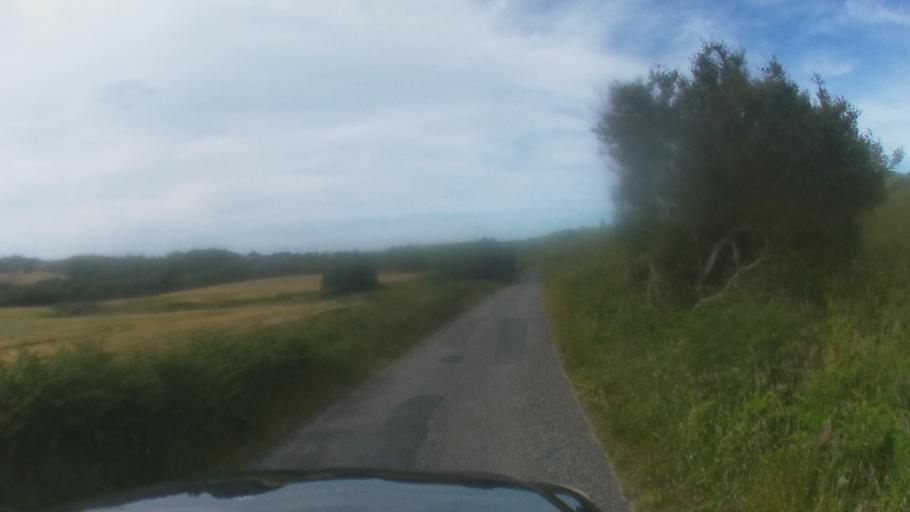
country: IE
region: Leinster
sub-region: Loch Garman
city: Castlebridge
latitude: 52.3922
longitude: -6.3632
